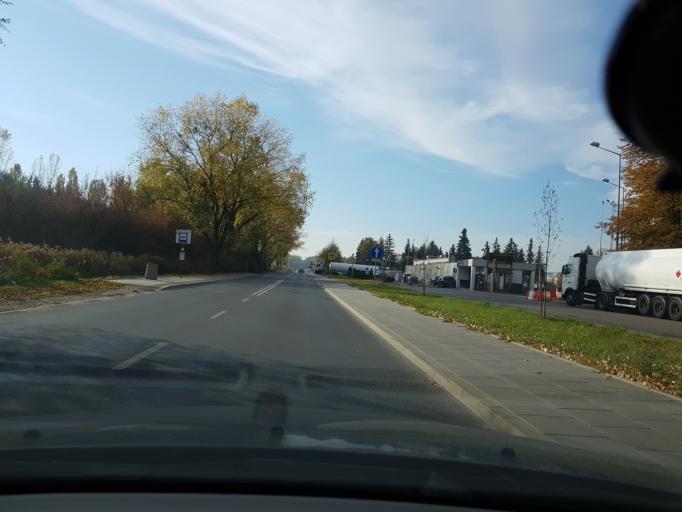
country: PL
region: Masovian Voivodeship
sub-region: Powiat warszawski zachodni
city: Babice
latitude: 52.2823
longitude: 20.8760
